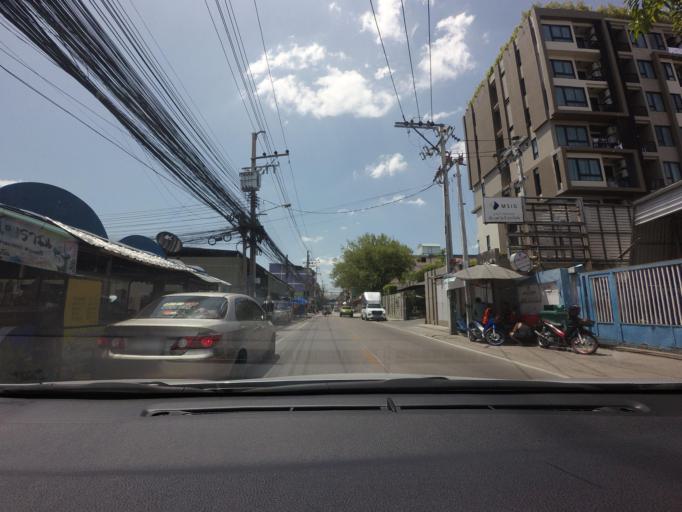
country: TH
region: Bangkok
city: Watthana
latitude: 13.7285
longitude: 100.6091
